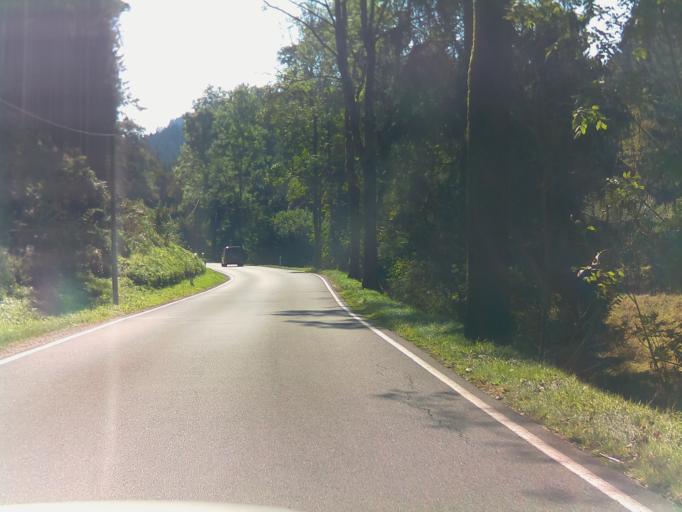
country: DE
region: Thuringia
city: Leutenberg
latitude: 50.5173
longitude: 11.4831
